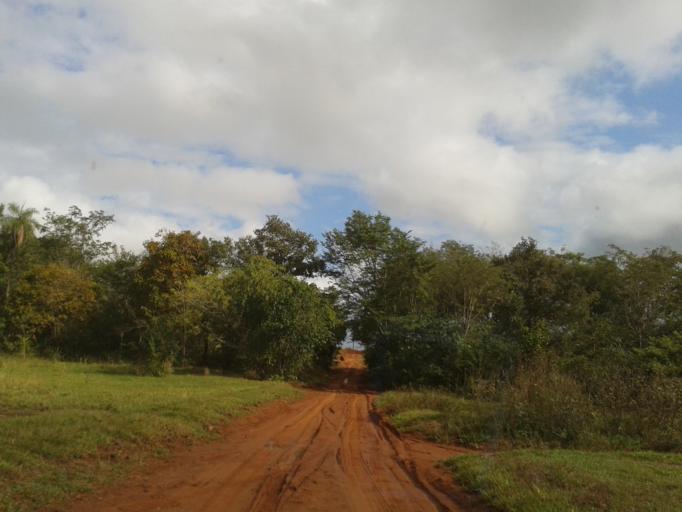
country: BR
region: Minas Gerais
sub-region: Campina Verde
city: Campina Verde
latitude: -19.4925
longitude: -49.6114
